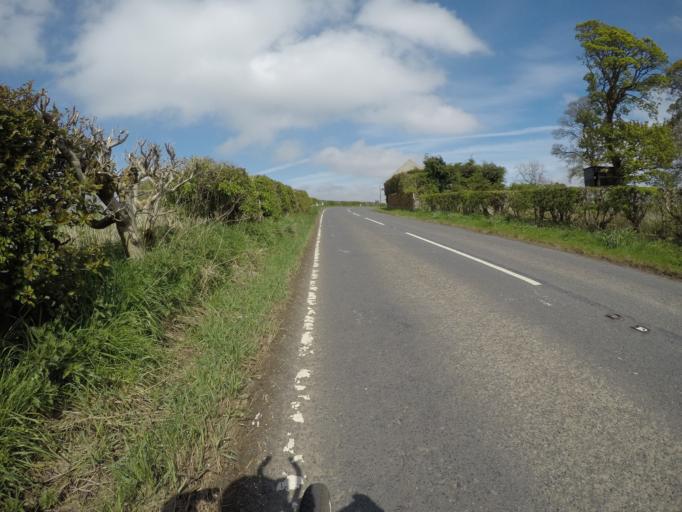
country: GB
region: Scotland
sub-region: East Ayrshire
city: Stewarton
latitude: 55.6885
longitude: -4.4990
